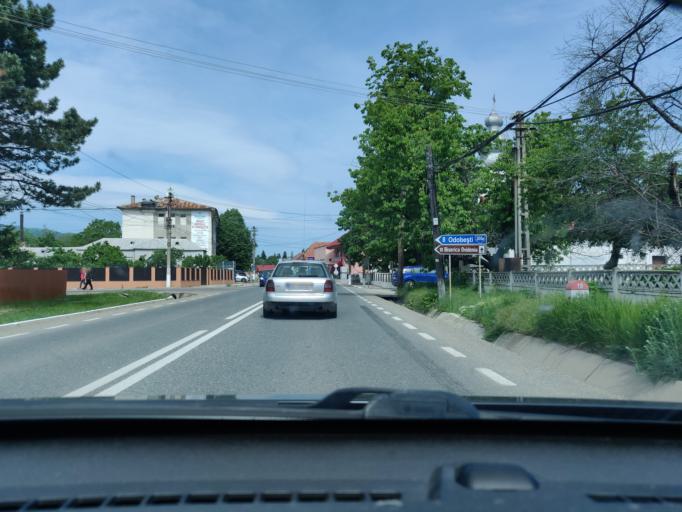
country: RO
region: Vrancea
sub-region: Comuna Bolotesti
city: Bolotesti
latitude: 45.8393
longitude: 27.0739
